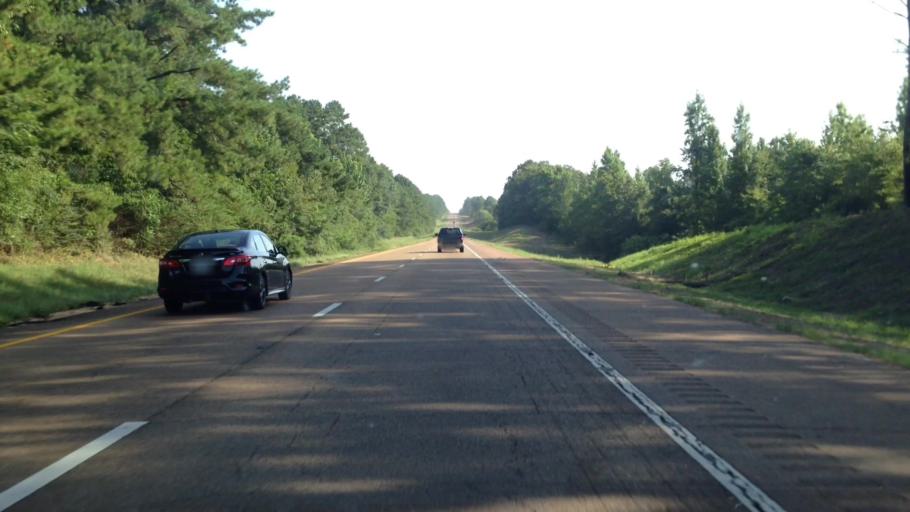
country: US
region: Mississippi
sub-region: Lincoln County
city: Brookhaven
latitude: 31.4519
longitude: -90.4791
